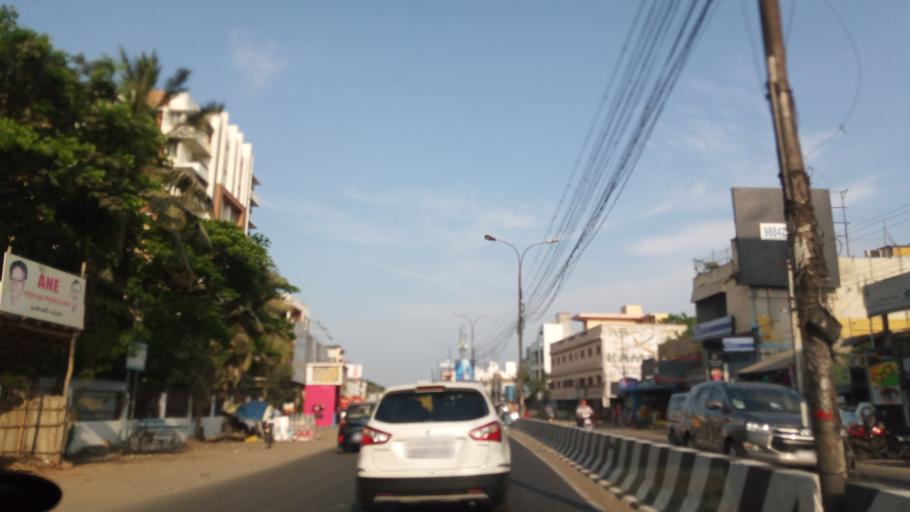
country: IN
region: Tamil Nadu
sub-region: Thiruvallur
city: Porur
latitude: 13.0377
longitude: 80.1364
